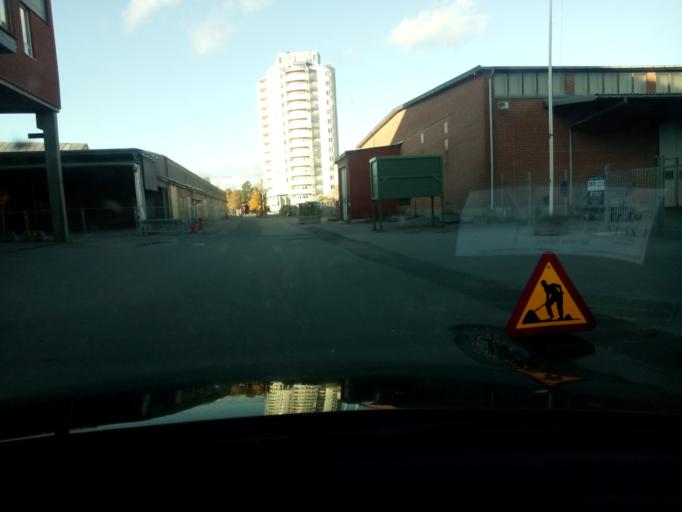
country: SE
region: Soedermanland
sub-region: Nykopings Kommun
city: Nykoping
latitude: 58.7451
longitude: 17.0151
